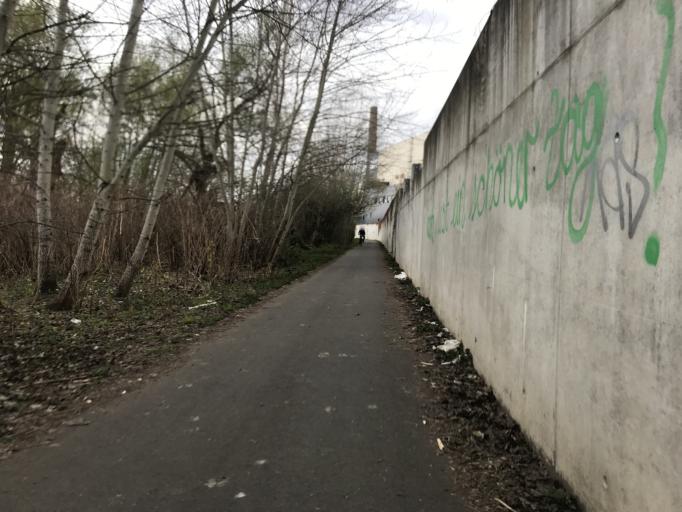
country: DE
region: Hesse
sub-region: Regierungsbezirk Darmstadt
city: Hochheim am Main
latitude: 50.0037
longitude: 8.3179
